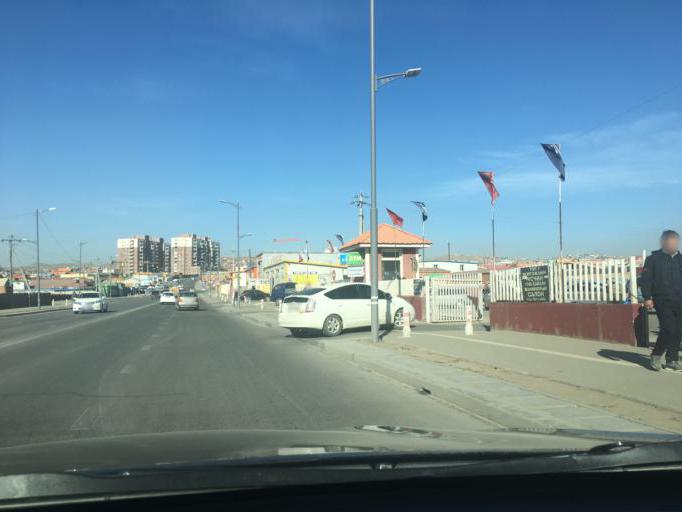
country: MN
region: Ulaanbaatar
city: Ulaanbaatar
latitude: 47.9119
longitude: 106.7835
